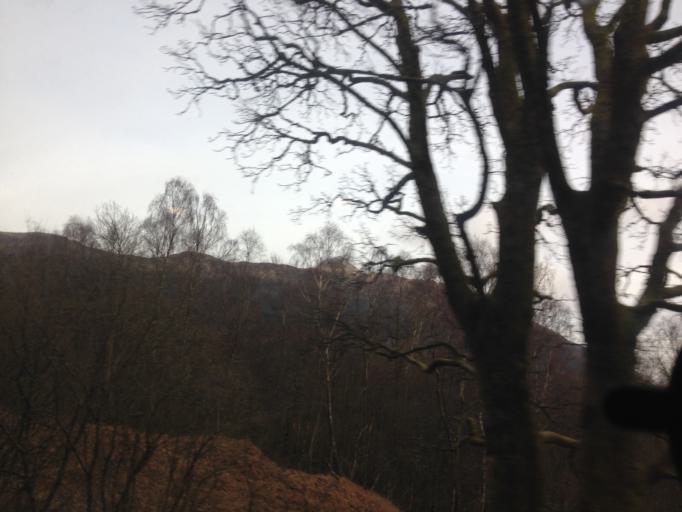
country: GB
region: Scotland
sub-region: Argyll and Bute
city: Garelochhead
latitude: 56.2087
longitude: -4.7065
